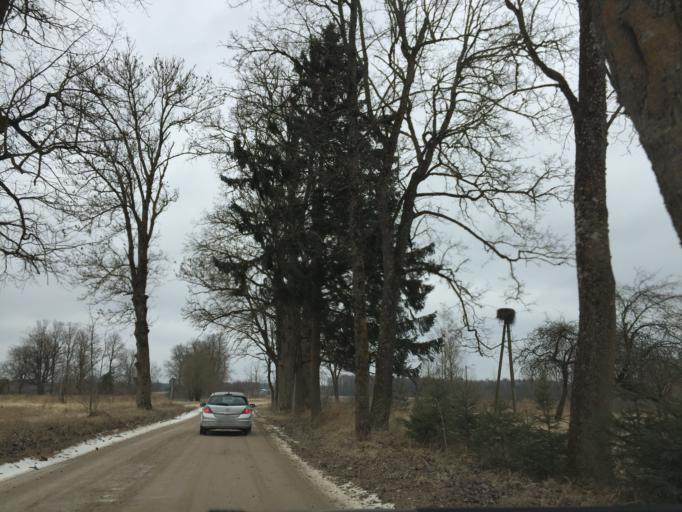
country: LV
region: Kegums
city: Kegums
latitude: 56.7687
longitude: 24.7724
